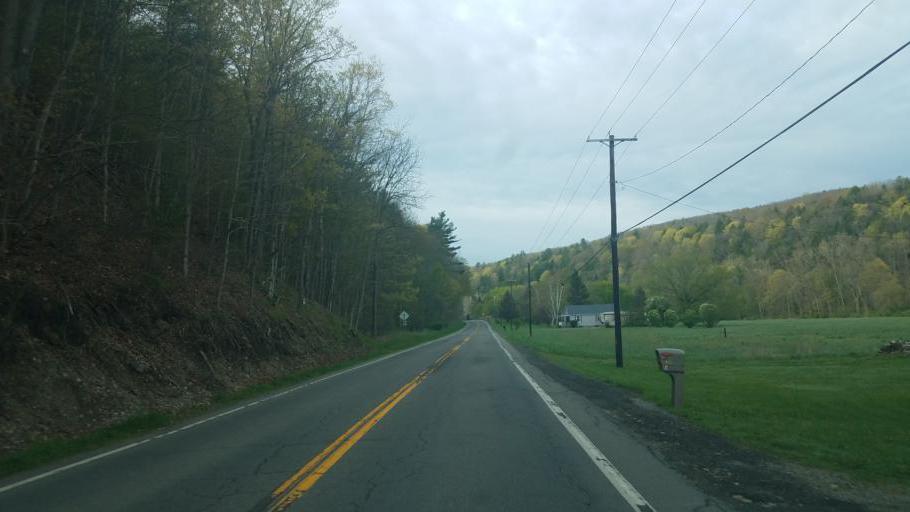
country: US
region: New York
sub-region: Steuben County
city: Canisteo
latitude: 42.2492
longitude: -77.5825
